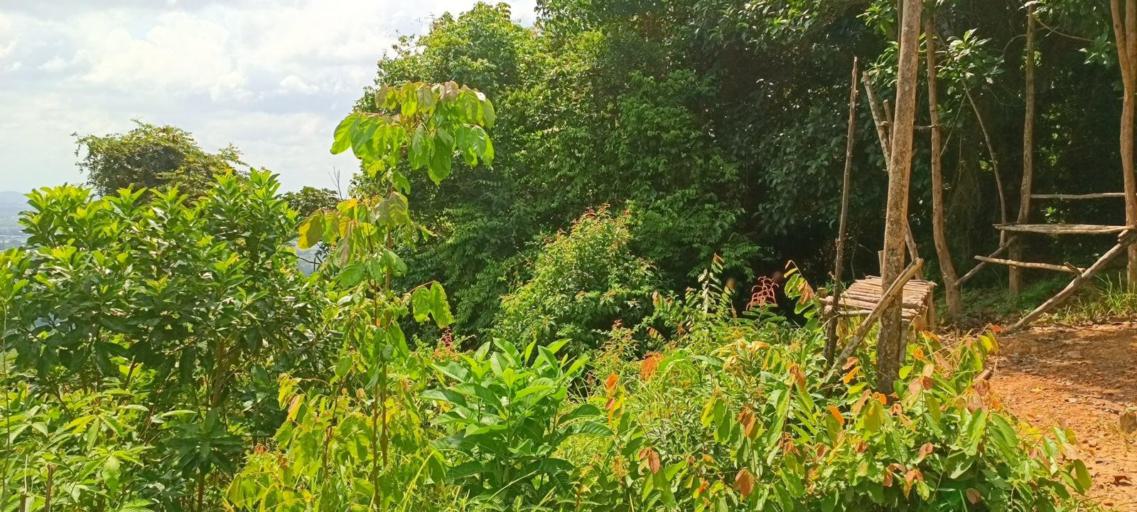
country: MY
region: Kedah
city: Sungai Petani
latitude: 5.6031
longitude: 100.4576
